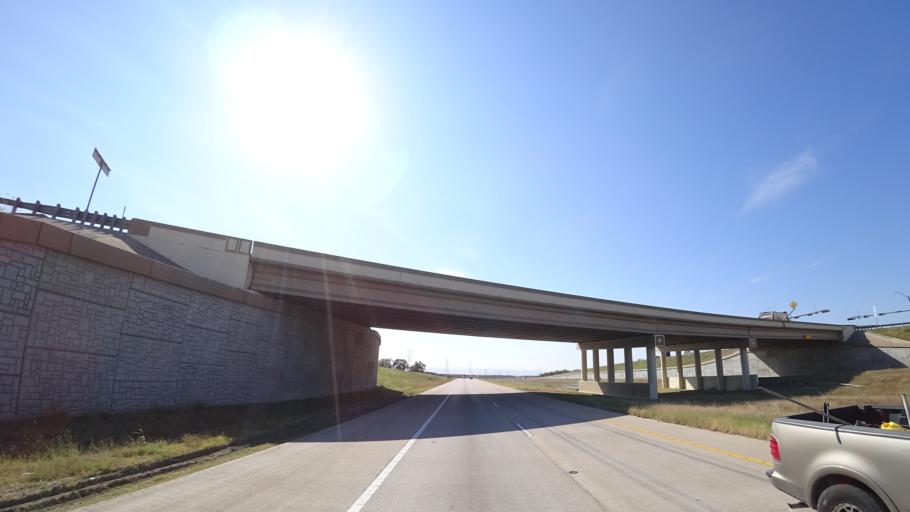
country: US
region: Texas
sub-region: Travis County
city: Hornsby Bend
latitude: 30.2881
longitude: -97.5754
